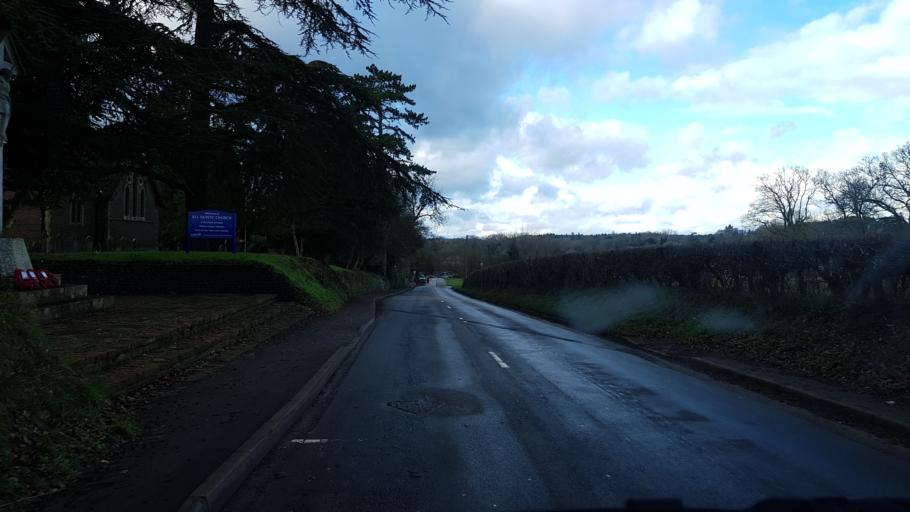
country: GB
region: England
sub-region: Surrey
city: Elstead
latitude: 51.1807
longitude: -0.7515
